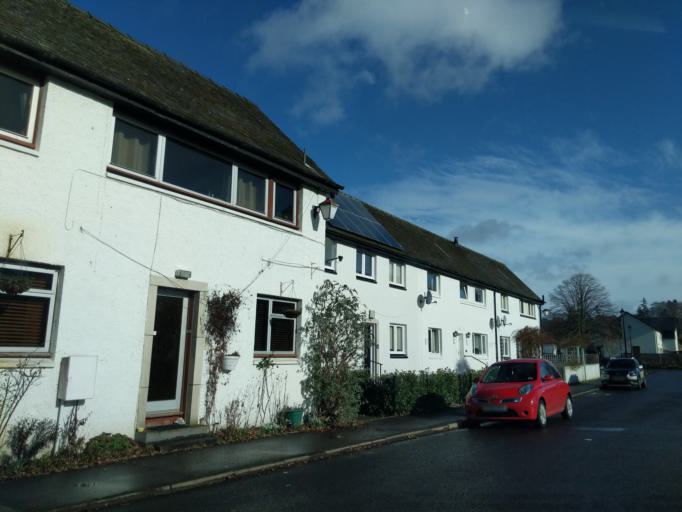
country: GB
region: Scotland
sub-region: Perth and Kinross
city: Aberfeldy
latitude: 56.5858
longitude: -3.9969
